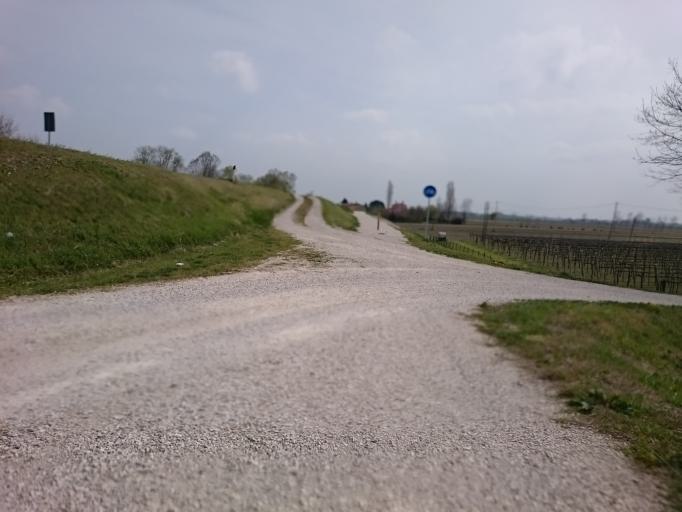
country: IT
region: Veneto
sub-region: Provincia di Padova
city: Campagnola
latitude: 45.2590
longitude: 11.9790
